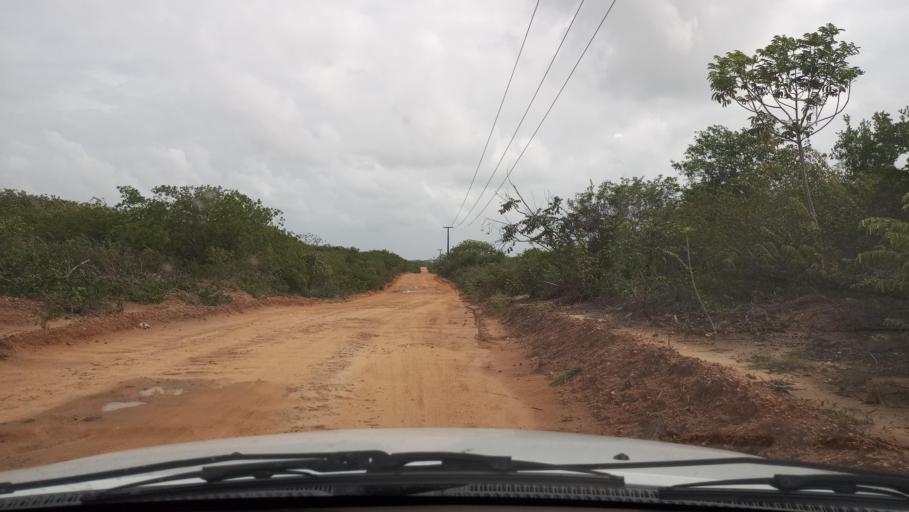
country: BR
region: Rio Grande do Norte
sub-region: Maxaranguape
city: Sao Miguel
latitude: -5.4803
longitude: -35.3030
